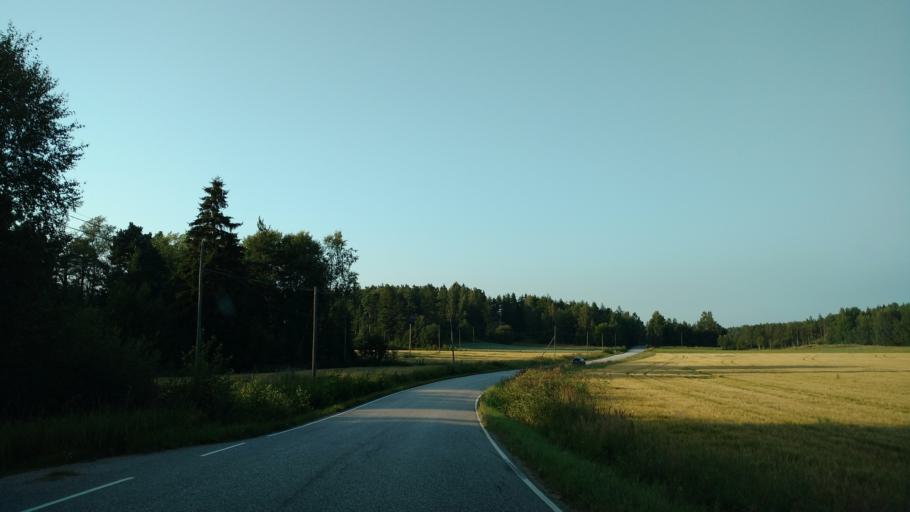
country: FI
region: Varsinais-Suomi
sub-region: Aboland-Turunmaa
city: Dragsfjaerd
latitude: 60.0399
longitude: 22.4440
